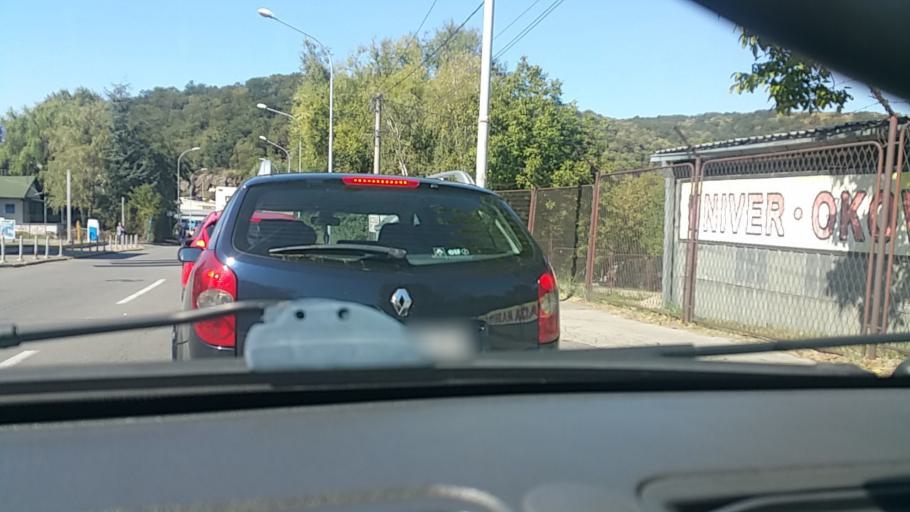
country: RS
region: Central Serbia
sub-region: Belgrade
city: Rakovica
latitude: 44.7509
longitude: 20.4487
